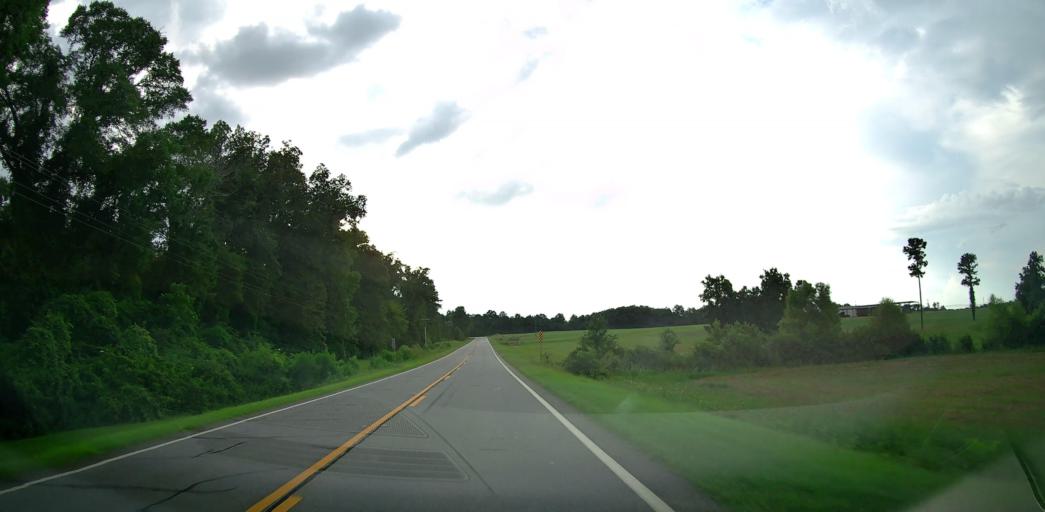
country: US
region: Georgia
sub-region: Pulaski County
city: Hawkinsville
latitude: 32.2937
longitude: -83.5174
